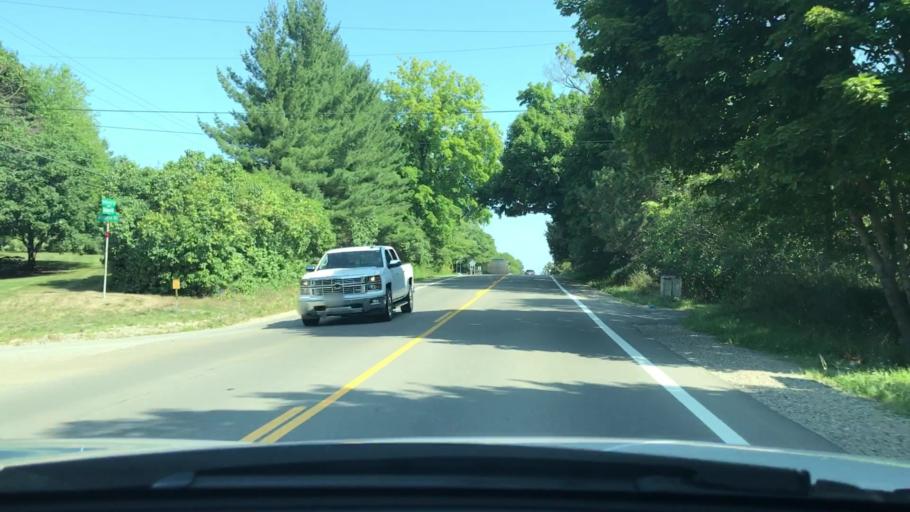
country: US
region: Michigan
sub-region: Oakland County
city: Oxford
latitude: 42.7977
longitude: -83.3331
